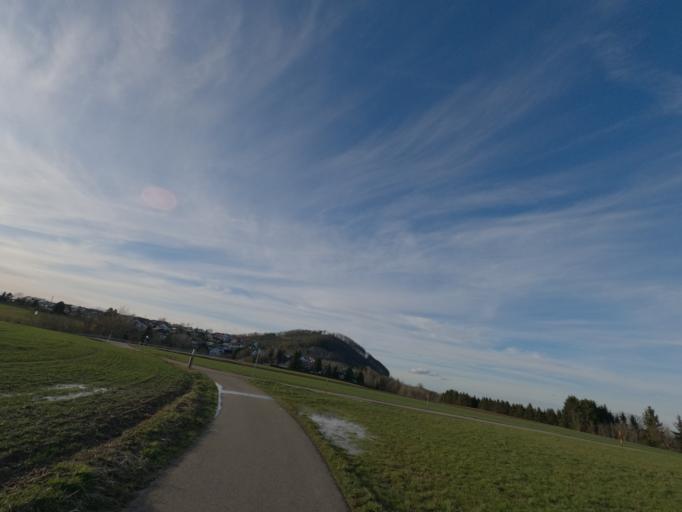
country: DE
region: Baden-Wuerttemberg
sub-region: Regierungsbezirk Stuttgart
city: Waldstetten
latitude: 48.7466
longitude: 9.8009
